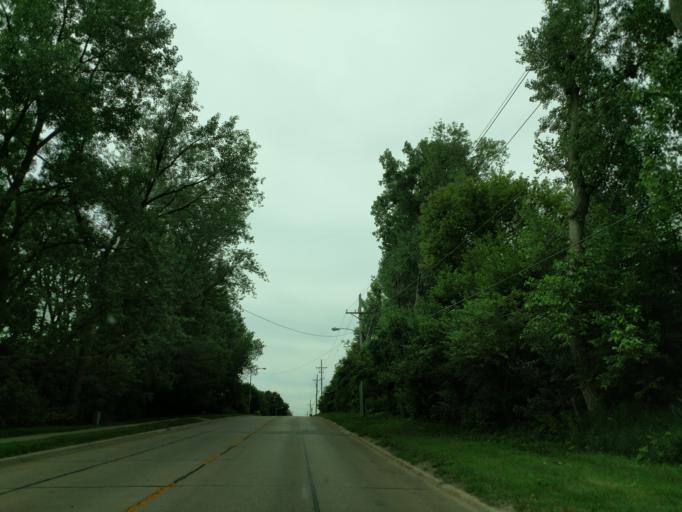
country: US
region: Nebraska
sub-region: Sarpy County
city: La Vista
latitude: 41.1961
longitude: -96.0334
